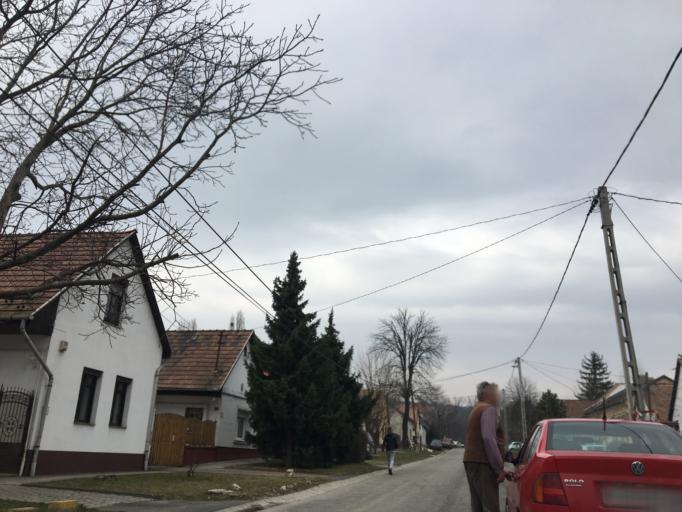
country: HU
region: Pest
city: Budakalasz
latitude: 47.6001
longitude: 19.0395
